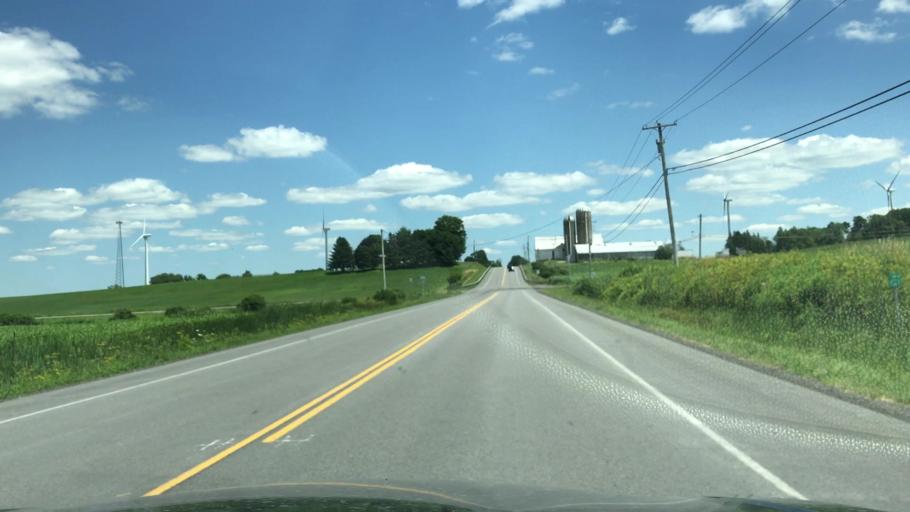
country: US
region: New York
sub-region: Erie County
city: Alden
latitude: 42.7700
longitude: -78.4207
